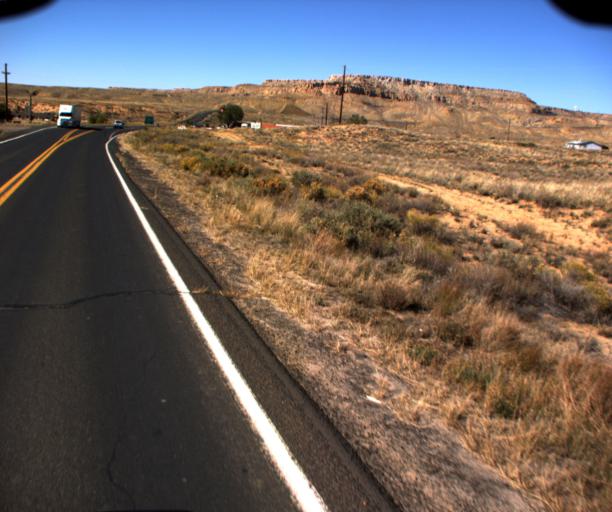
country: US
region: Arizona
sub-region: Navajo County
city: First Mesa
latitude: 35.7931
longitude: -110.5028
